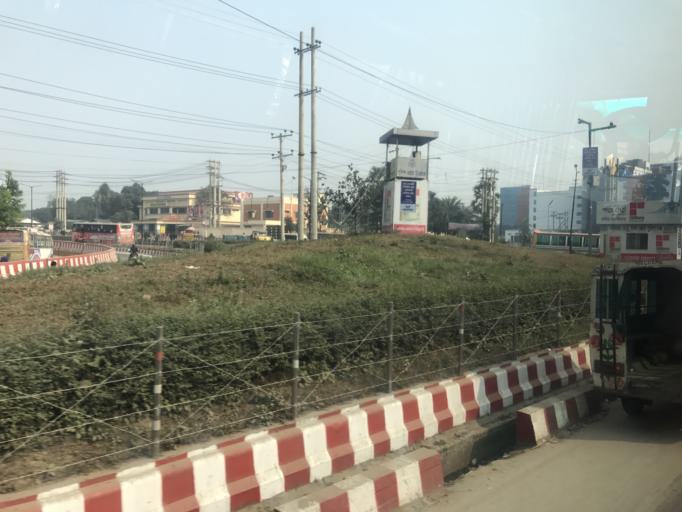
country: BD
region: Dhaka
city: Tungi
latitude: 23.9138
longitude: 90.2580
